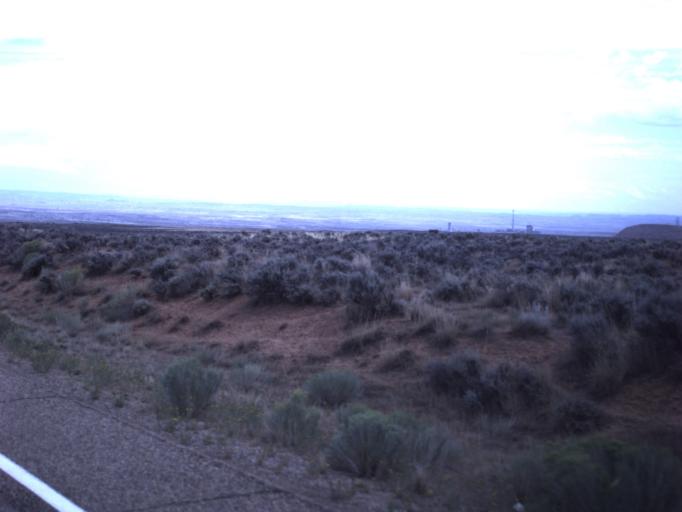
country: US
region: Utah
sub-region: Uintah County
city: Naples
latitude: 40.1493
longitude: -109.2962
